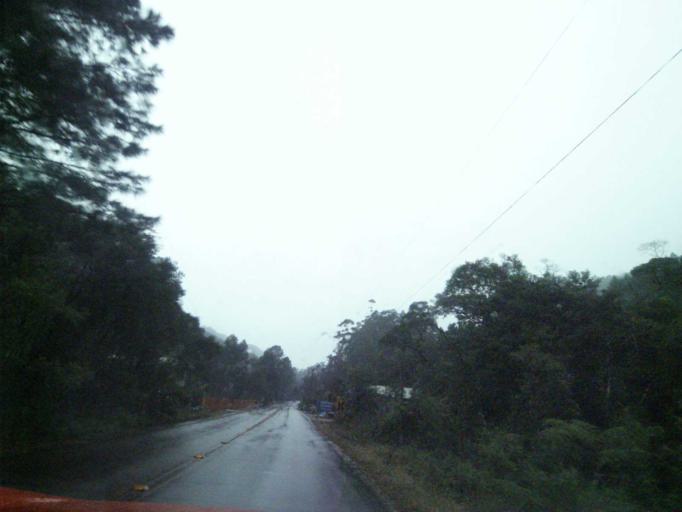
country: BR
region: Santa Catarina
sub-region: Anitapolis
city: Anitapolis
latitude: -27.7858
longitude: -49.0430
